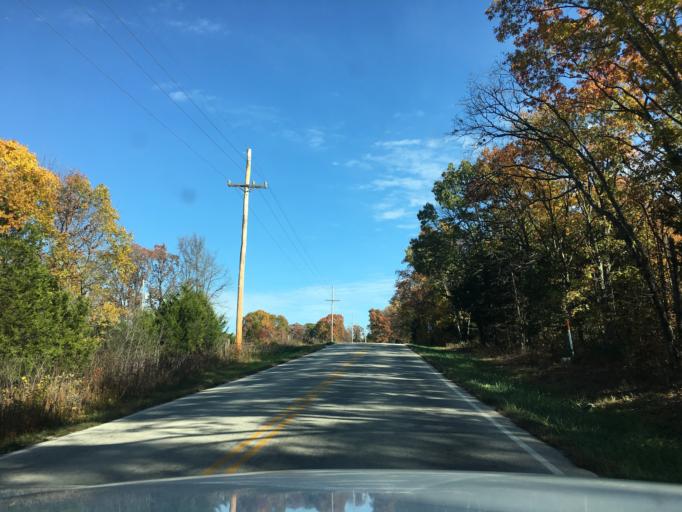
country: US
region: Missouri
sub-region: Maries County
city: Belle
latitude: 38.3369
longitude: -91.7669
